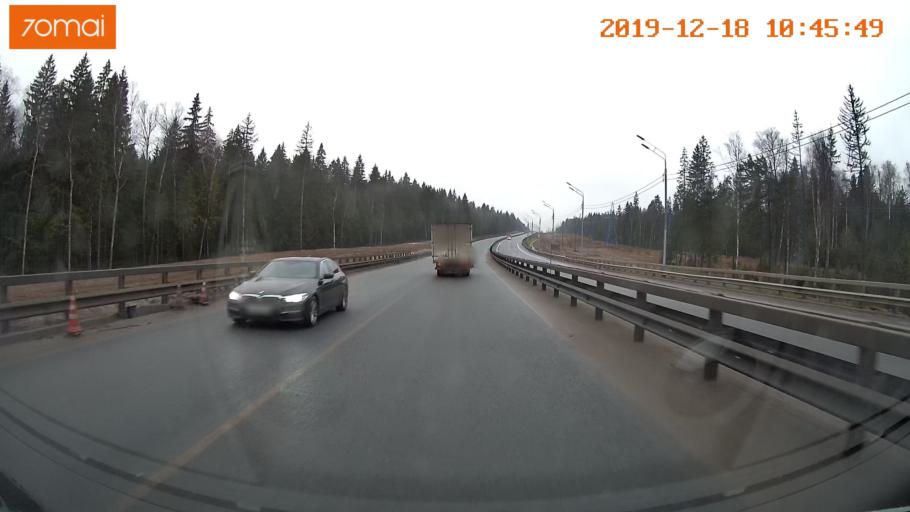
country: RU
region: Moskovskaya
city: Aprelevka
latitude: 55.4800
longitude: 37.0558
